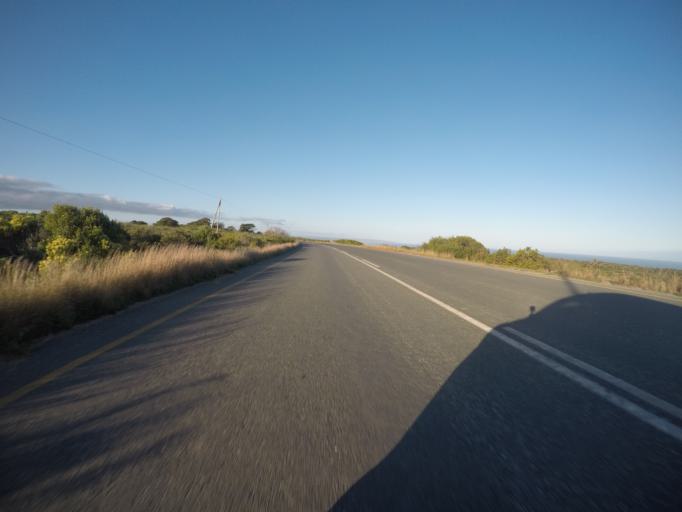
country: ZA
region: Western Cape
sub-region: Eden District Municipality
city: Riversdale
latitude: -34.3940
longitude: 21.3916
